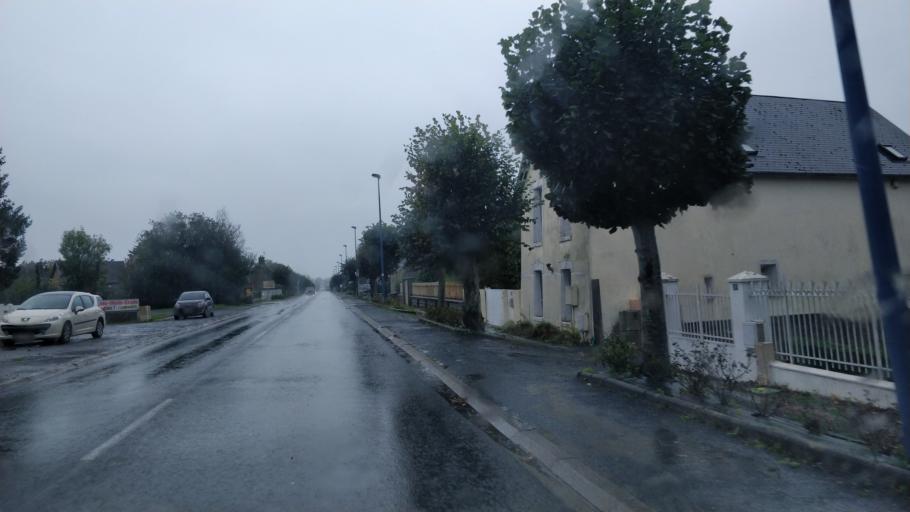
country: FR
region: Lower Normandy
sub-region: Departement de la Manche
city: Brehal
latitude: 48.8945
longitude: -1.5145
